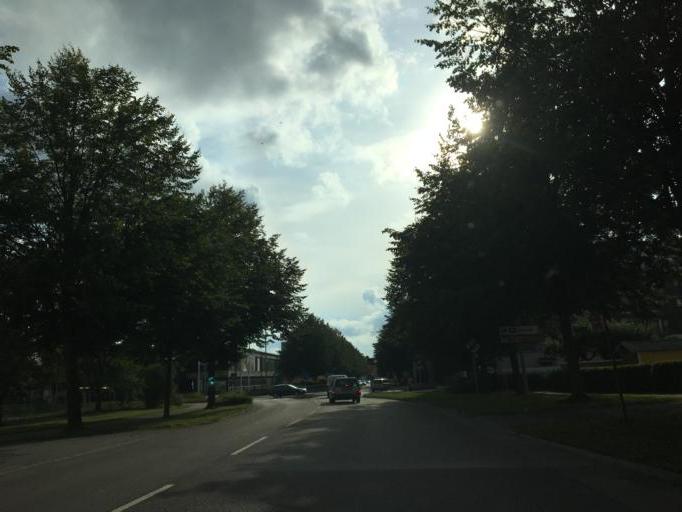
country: SE
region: Uppsala
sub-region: Enkopings Kommun
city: Enkoping
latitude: 59.6346
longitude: 17.0830
